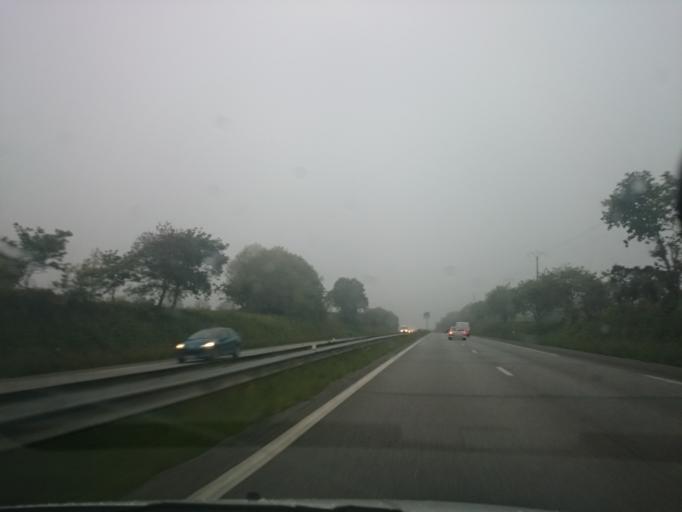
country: FR
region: Brittany
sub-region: Departement du Finistere
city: Briec
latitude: 48.1149
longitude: -4.0249
